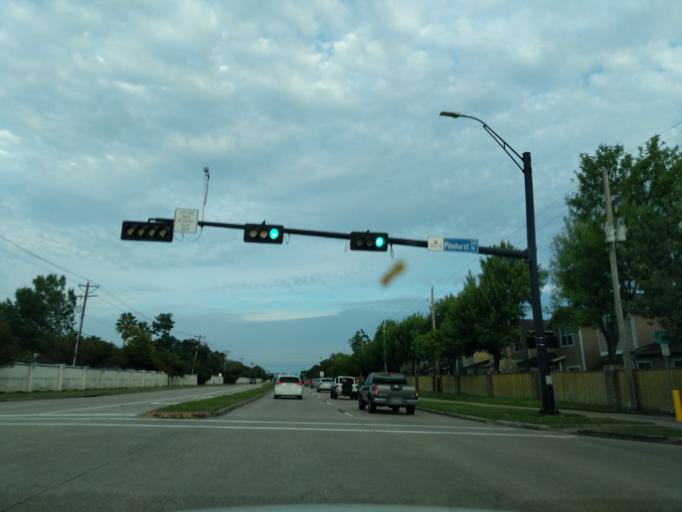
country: US
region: Texas
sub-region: Harris County
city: Nassau Bay
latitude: 29.5247
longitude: -95.0617
